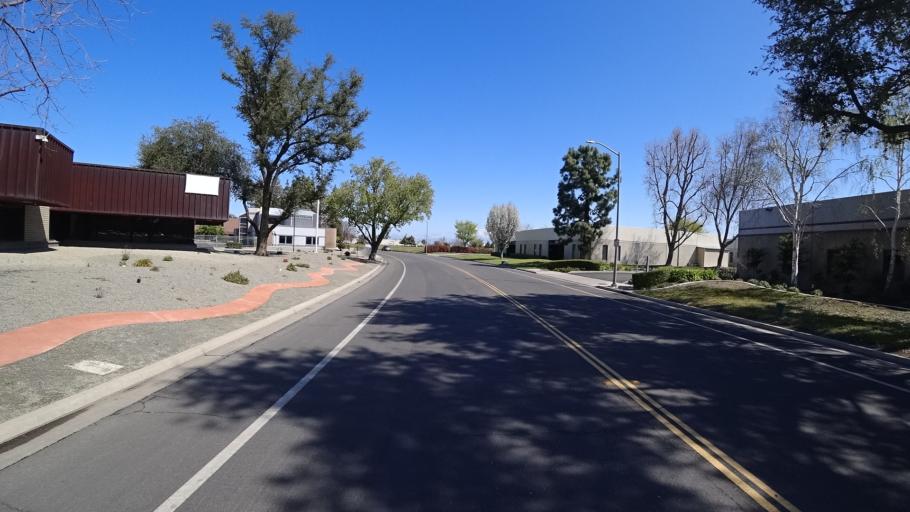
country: US
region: California
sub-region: Fresno County
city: Tarpey Village
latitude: 36.7701
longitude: -119.7275
